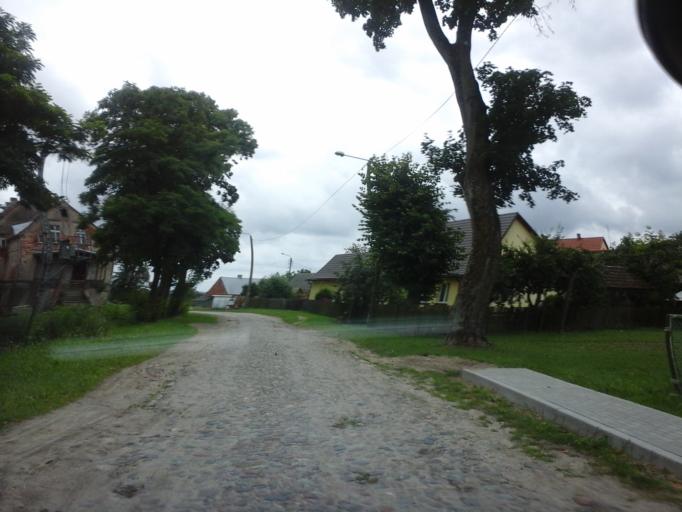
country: PL
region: West Pomeranian Voivodeship
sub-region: Powiat choszczenski
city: Bierzwnik
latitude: 52.9908
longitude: 15.6315
